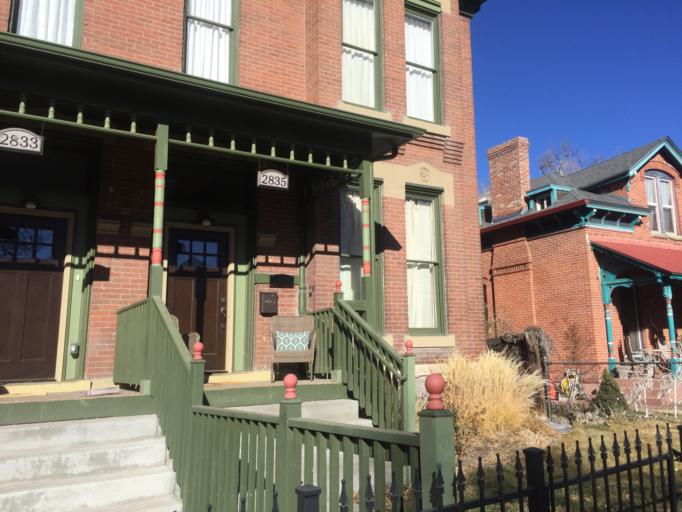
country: US
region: Colorado
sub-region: Denver County
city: Denver
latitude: 39.7590
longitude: -104.9798
